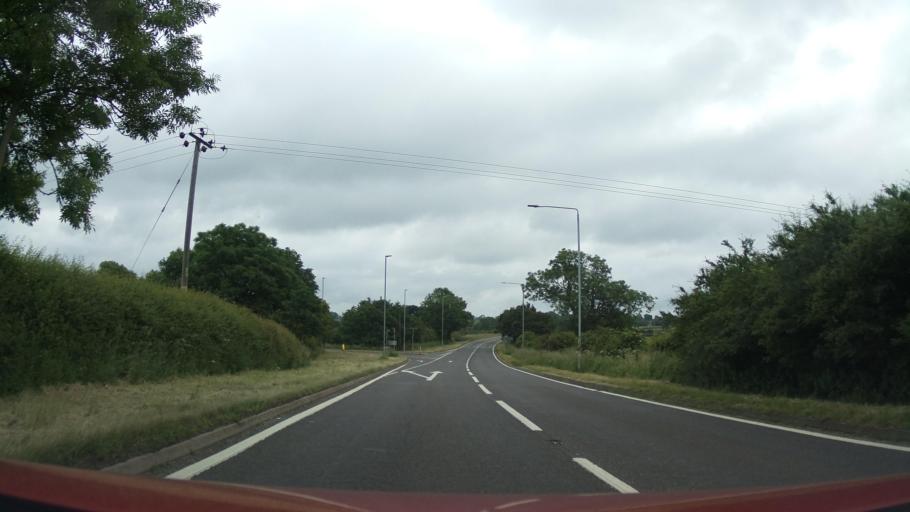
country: GB
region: England
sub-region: Leicestershire
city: Houghton on the Hill
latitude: 52.6238
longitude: -0.9703
